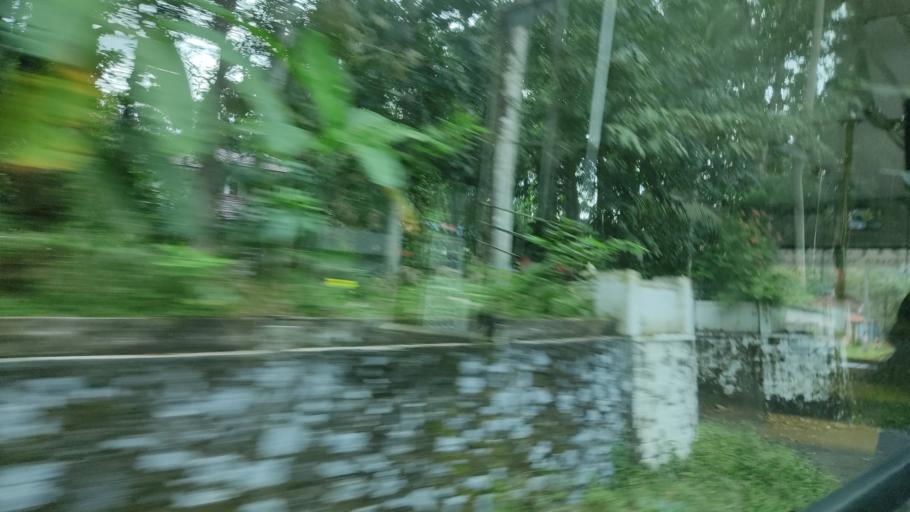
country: IN
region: Kerala
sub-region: Kottayam
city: Lalam
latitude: 9.6450
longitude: 76.7274
